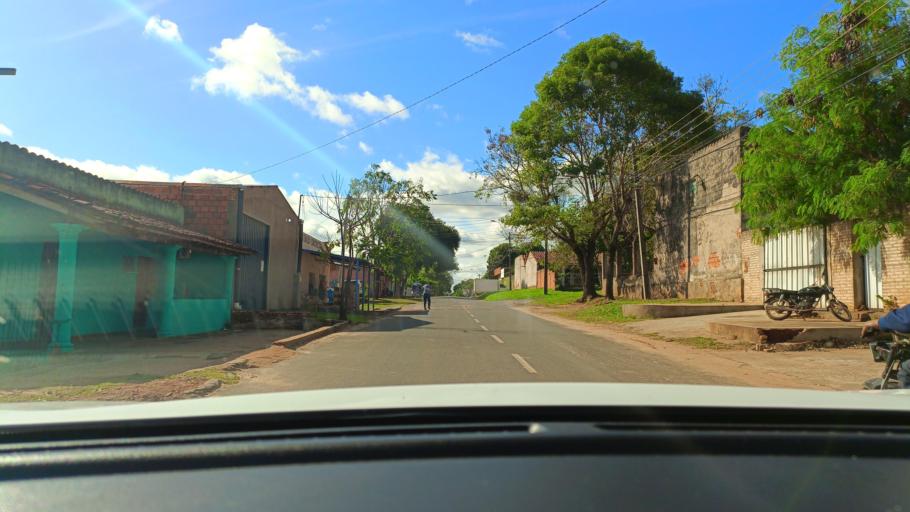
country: PY
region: San Pedro
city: Guayaybi
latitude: -24.6731
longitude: -56.4472
